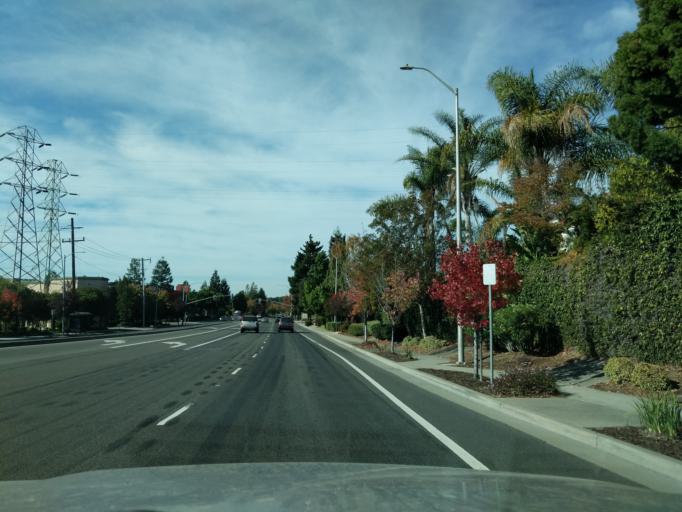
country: US
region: California
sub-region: Alameda County
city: Fremont
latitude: 37.5490
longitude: -121.9383
